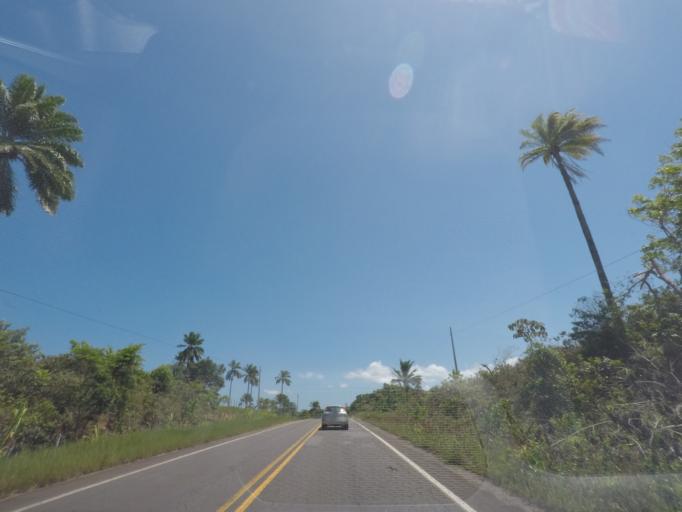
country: BR
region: Bahia
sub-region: Valenca
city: Valenca
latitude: -13.3016
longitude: -39.0356
